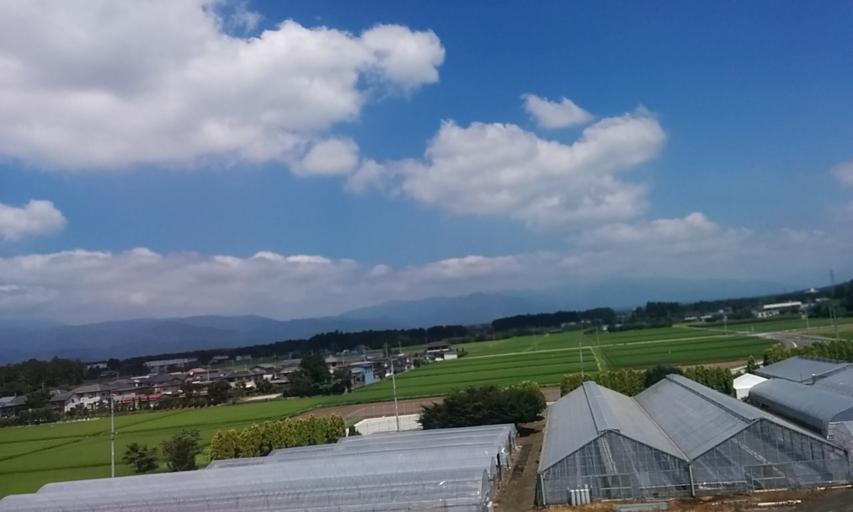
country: JP
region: Tochigi
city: Otawara
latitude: 36.8586
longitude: 139.9683
